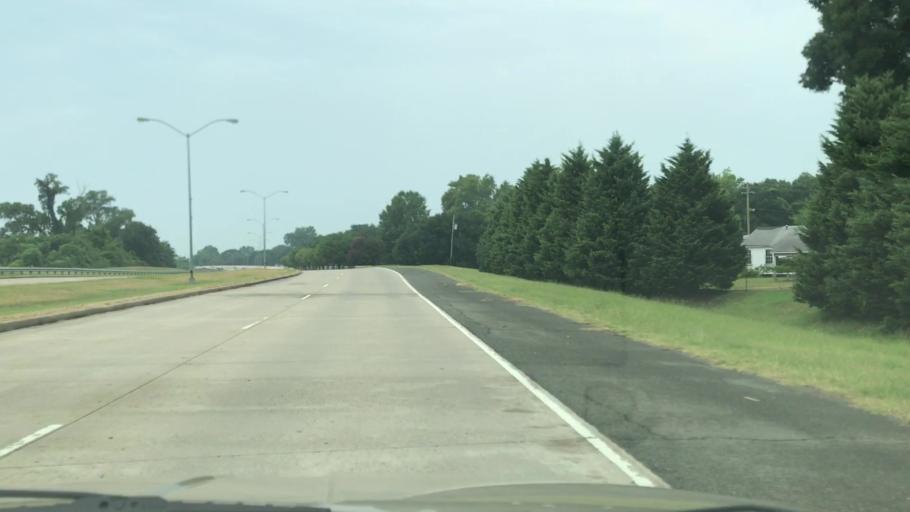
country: US
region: Louisiana
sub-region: Bossier Parish
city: Bossier City
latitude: 32.5063
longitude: -93.7117
